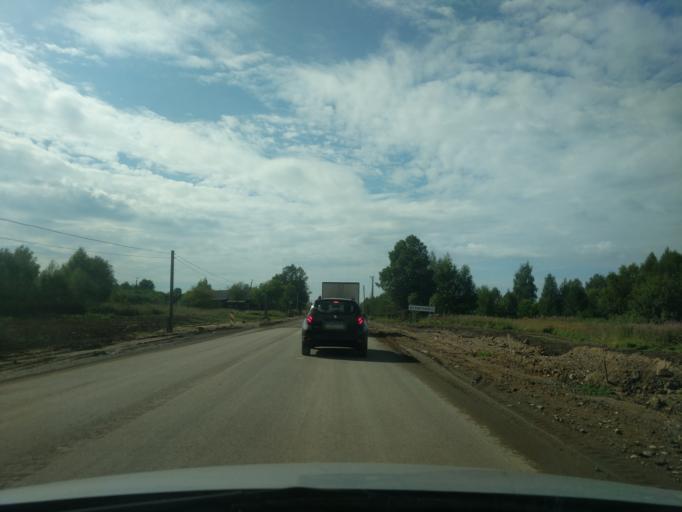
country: RU
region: Kostroma
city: Sudislavl'
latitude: 57.8718
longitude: 41.6545
